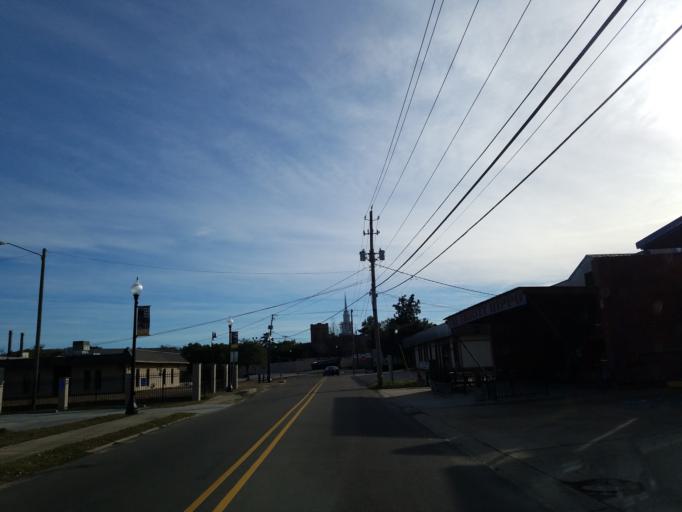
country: US
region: Mississippi
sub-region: Forrest County
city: Hattiesburg
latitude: 31.3256
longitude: -89.2944
